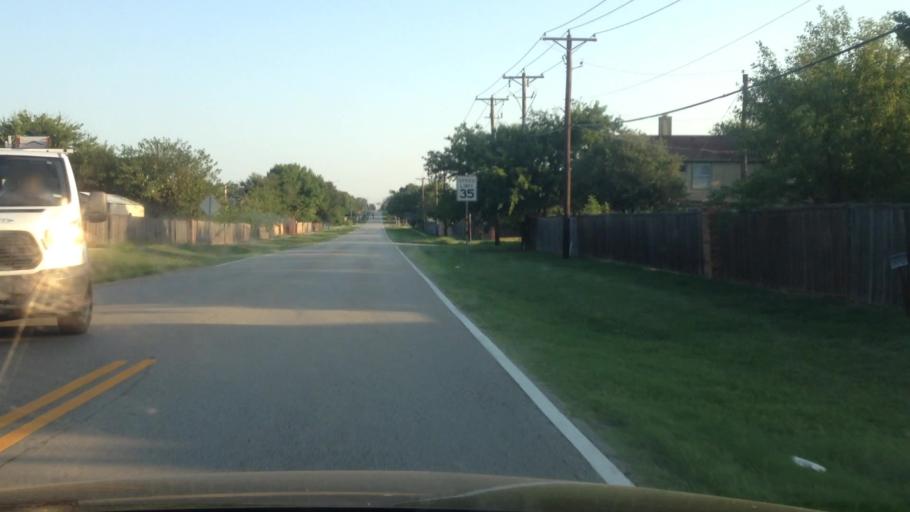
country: US
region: Texas
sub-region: Tarrant County
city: Dalworthington Gardens
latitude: 32.6522
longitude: -97.1023
